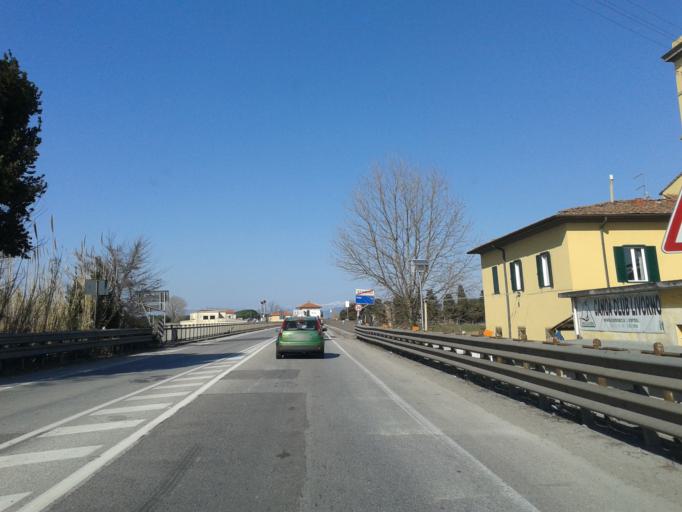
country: IT
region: Tuscany
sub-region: Provincia di Livorno
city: Guasticce
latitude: 43.5987
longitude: 10.3519
